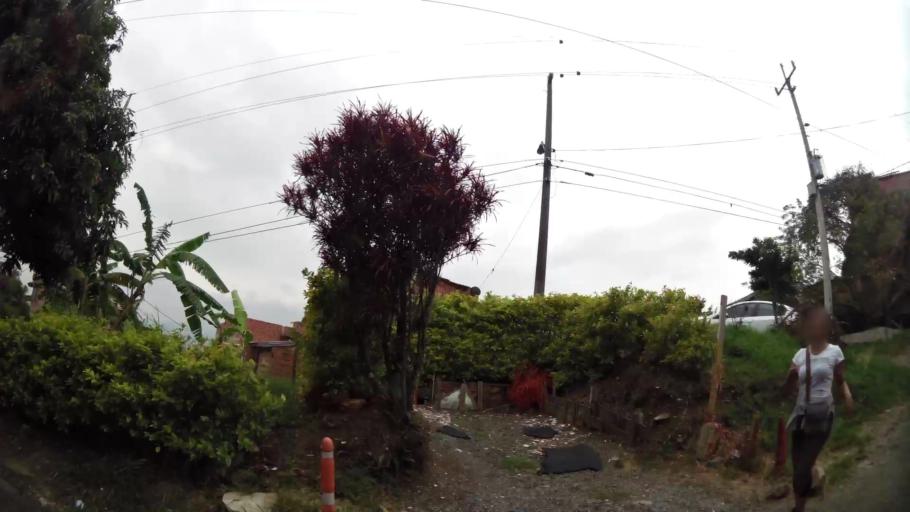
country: CO
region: Antioquia
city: Medellin
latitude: 6.2811
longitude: -75.5905
